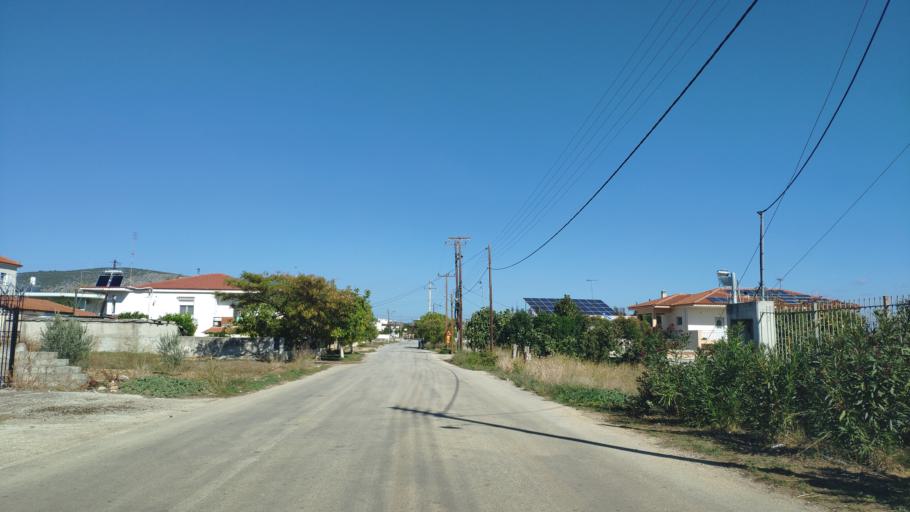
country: GR
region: Peloponnese
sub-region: Nomos Korinthias
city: Khiliomodhi
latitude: 37.8032
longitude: 22.8695
